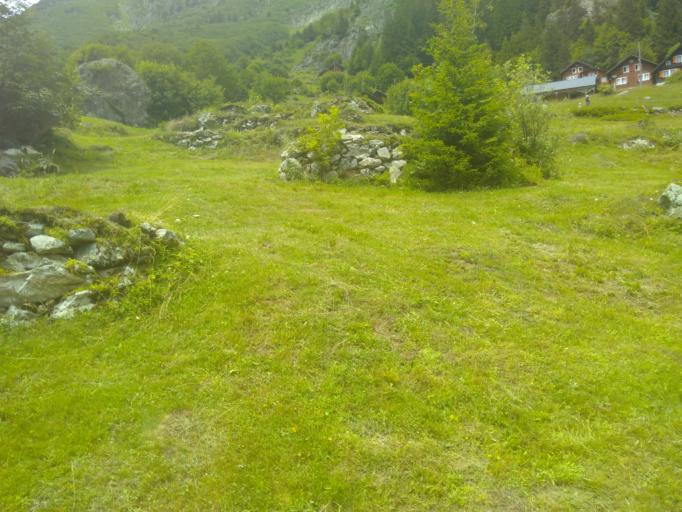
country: CH
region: Uri
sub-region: Uri
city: Silenen
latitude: 46.7763
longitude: 8.7258
